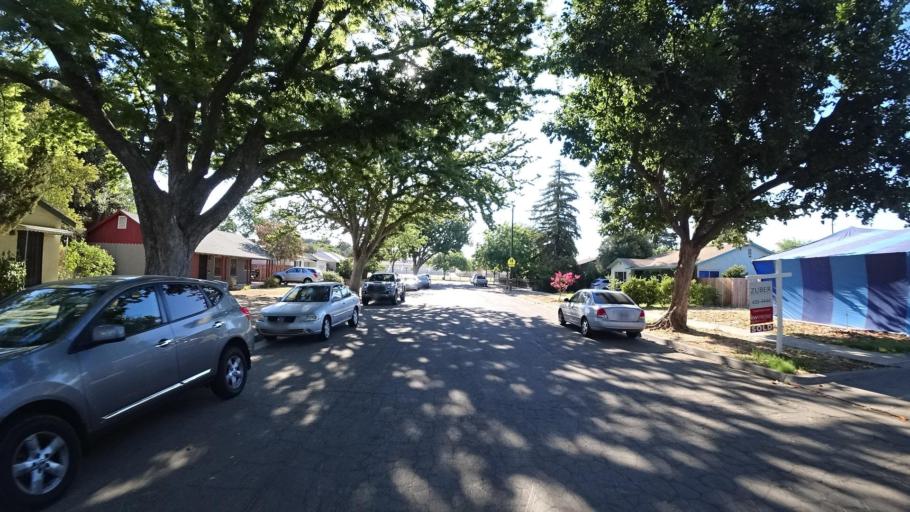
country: US
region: California
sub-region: Fresno County
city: Fresno
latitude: 36.7713
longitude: -119.8140
